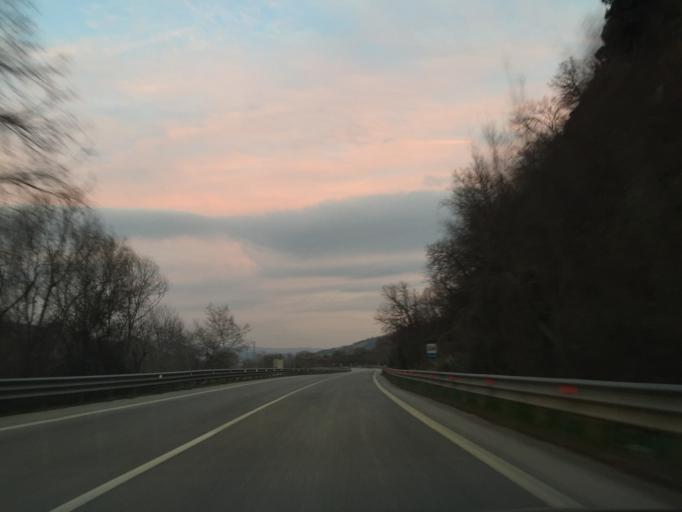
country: IT
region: Molise
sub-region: Provincia di Campobasso
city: Gambatesa
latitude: 41.5295
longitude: 14.8952
